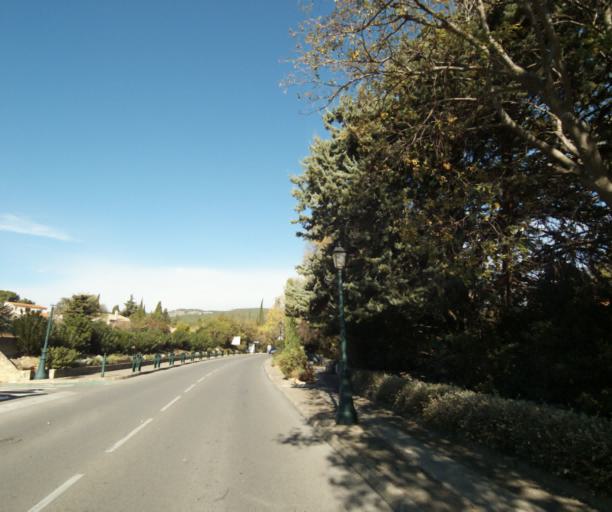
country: FR
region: Provence-Alpes-Cote d'Azur
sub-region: Departement des Bouches-du-Rhone
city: Ceyreste
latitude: 43.2107
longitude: 5.6289
